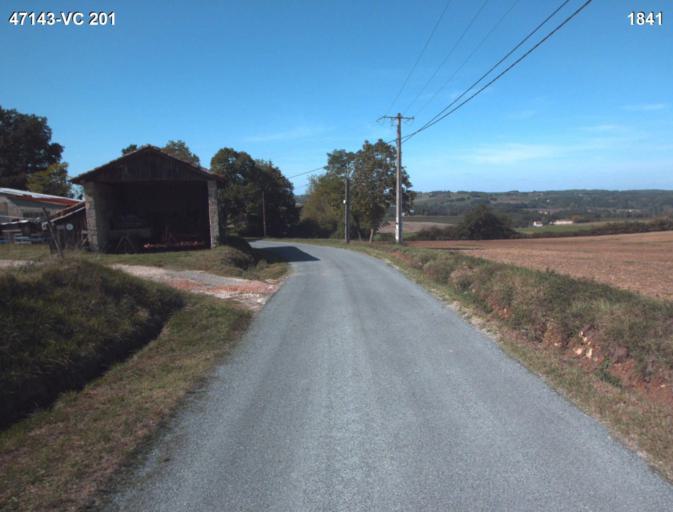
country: FR
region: Aquitaine
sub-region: Departement du Lot-et-Garonne
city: Vianne
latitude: 44.1850
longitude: 0.3295
